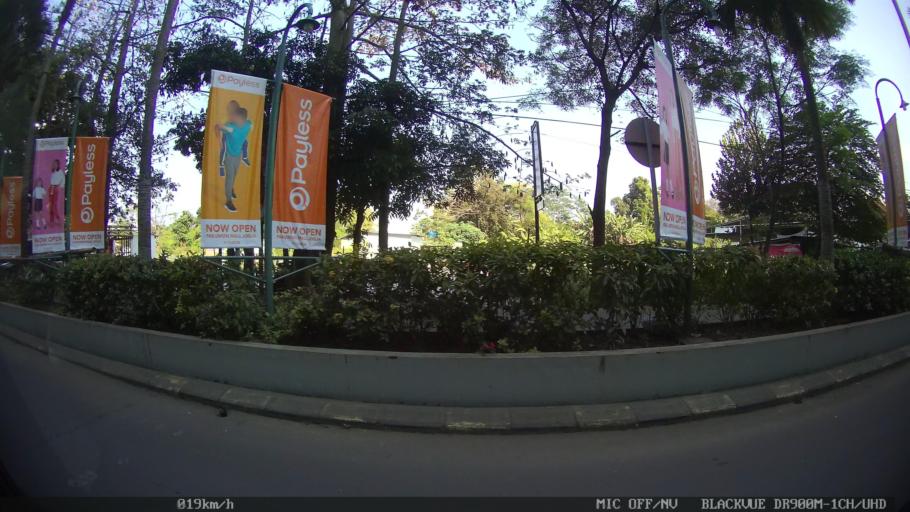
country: ID
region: Daerah Istimewa Yogyakarta
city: Depok
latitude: -7.7592
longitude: 110.3985
